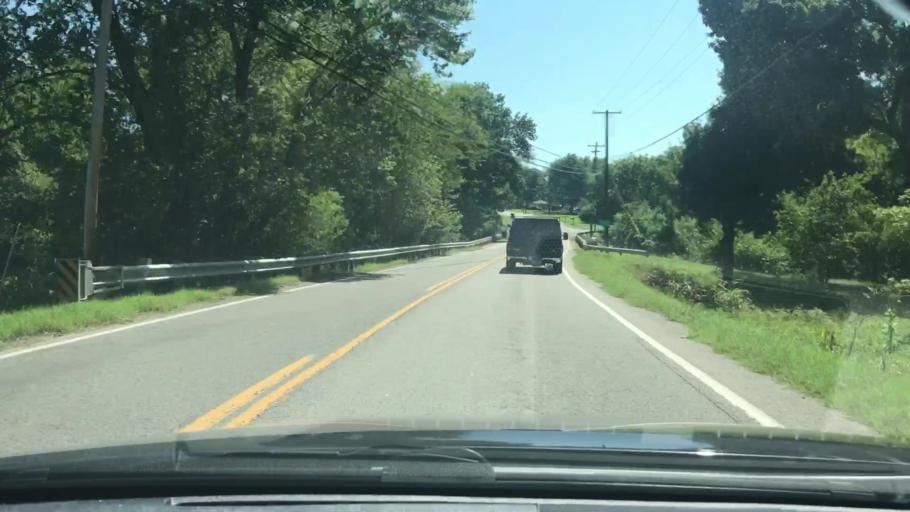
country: US
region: Tennessee
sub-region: Sumner County
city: Gallatin
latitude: 36.3950
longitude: -86.4697
